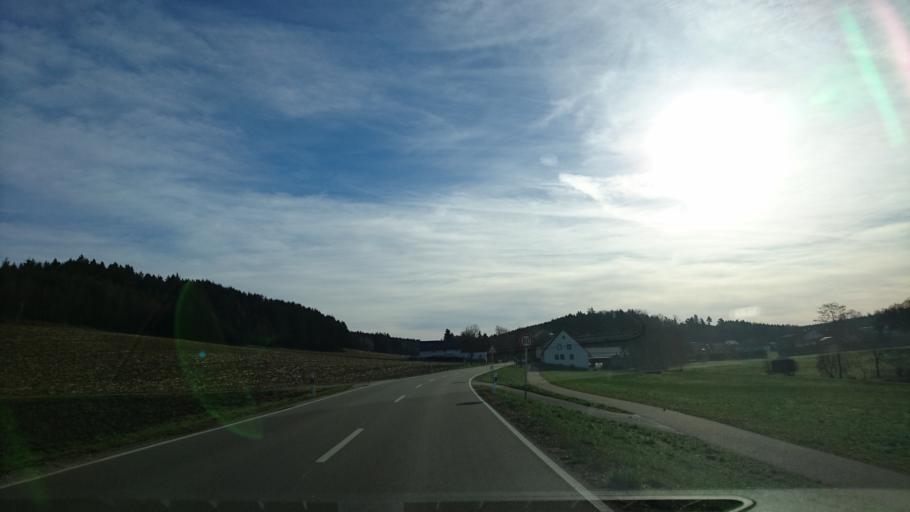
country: DE
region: Bavaria
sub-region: Swabia
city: Laugna
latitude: 48.5249
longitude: 10.7230
